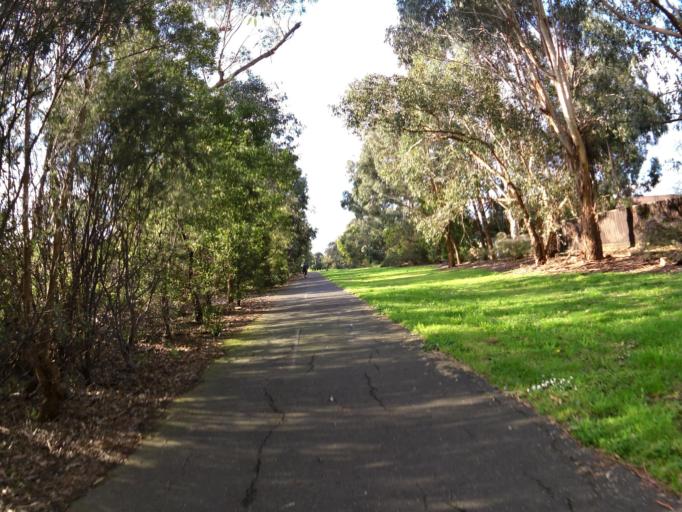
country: AU
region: Victoria
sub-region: Maroondah
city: Bayswater North
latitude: -37.8356
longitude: 145.3018
